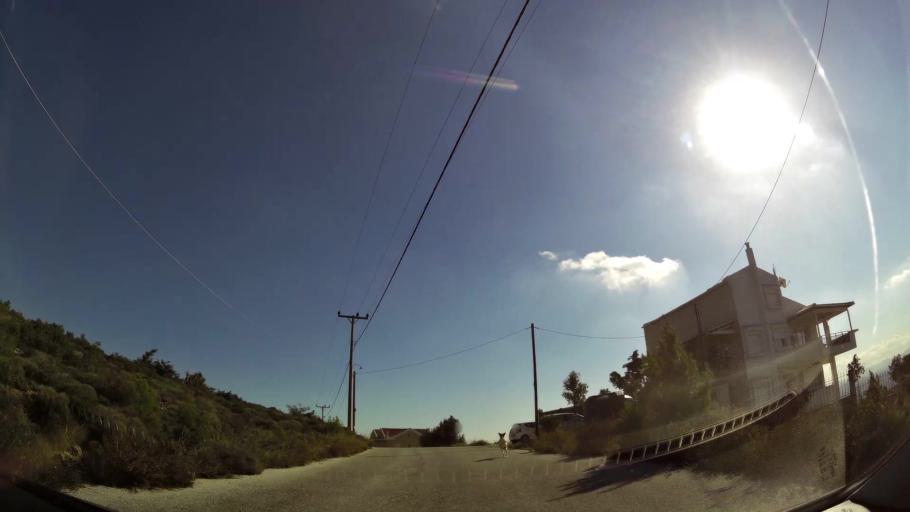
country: GR
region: Attica
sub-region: Nomarchia Anatolikis Attikis
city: Dioni
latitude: 38.0377
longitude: 23.9272
